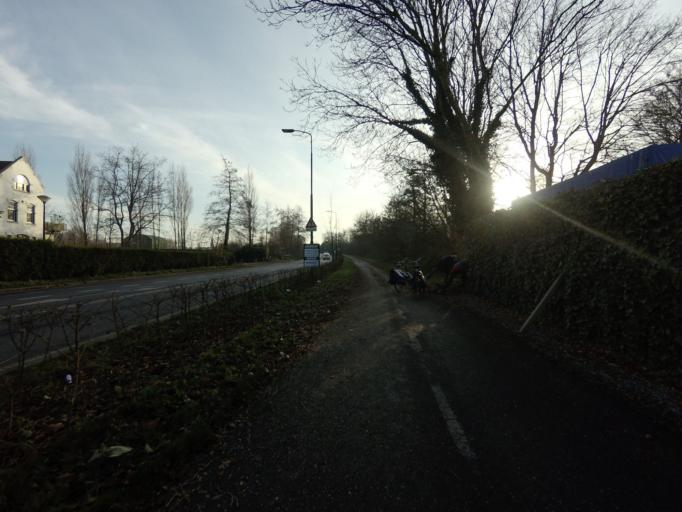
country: NL
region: Utrecht
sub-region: Gemeente De Ronde Venen
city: Mijdrecht
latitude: 52.2063
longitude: 4.8682
